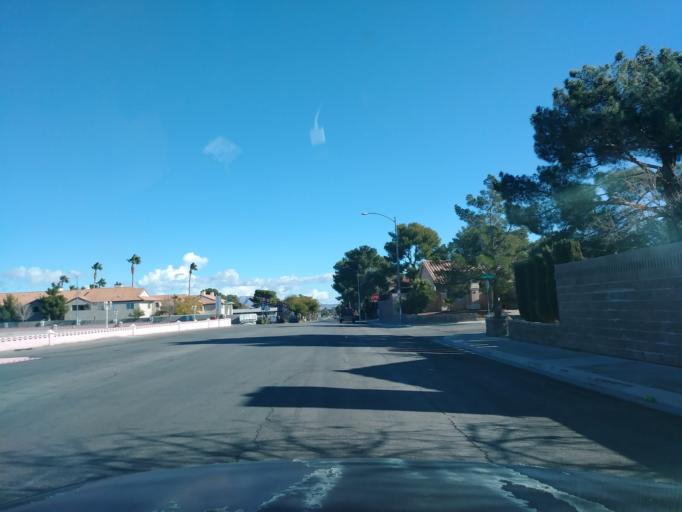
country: US
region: Nevada
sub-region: Clark County
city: Spring Valley
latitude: 36.1481
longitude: -115.2134
